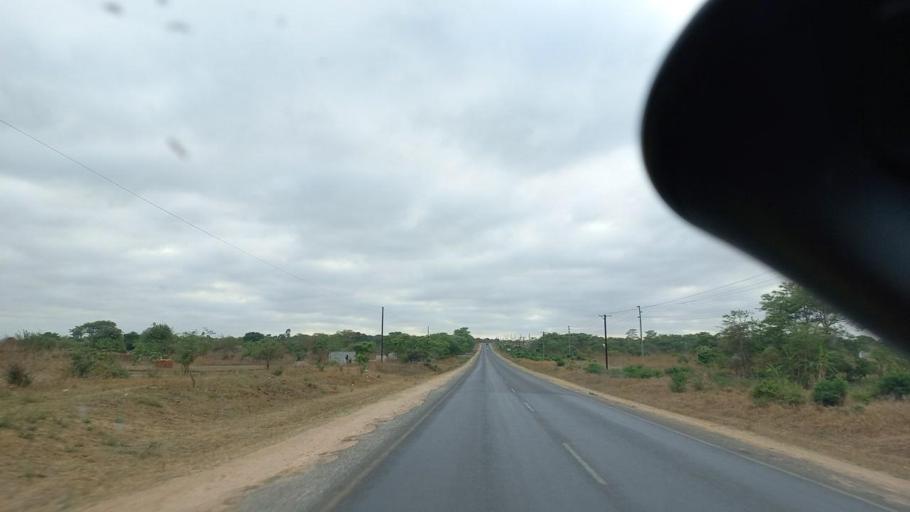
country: ZM
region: Lusaka
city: Chongwe
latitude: -15.3404
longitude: 28.6280
